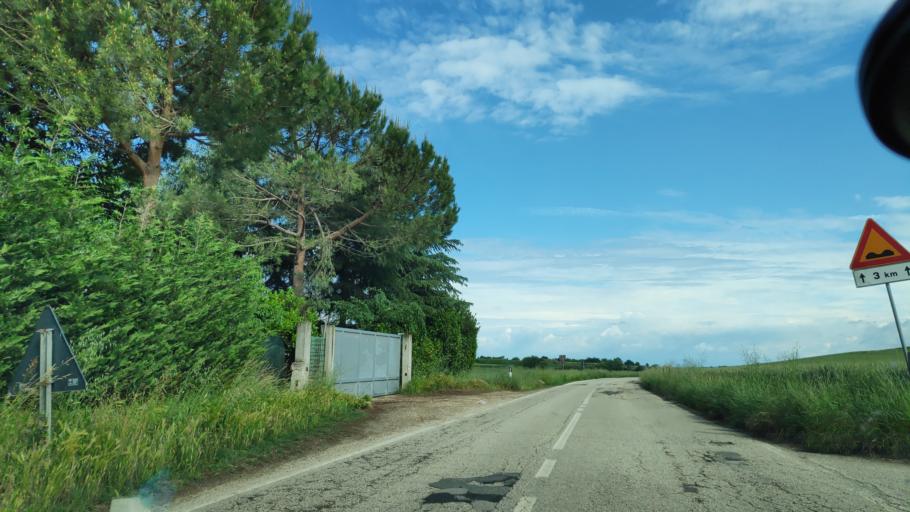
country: IT
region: Piedmont
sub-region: Provincia di Torino
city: Cambiano
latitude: 44.9917
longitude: 7.7752
